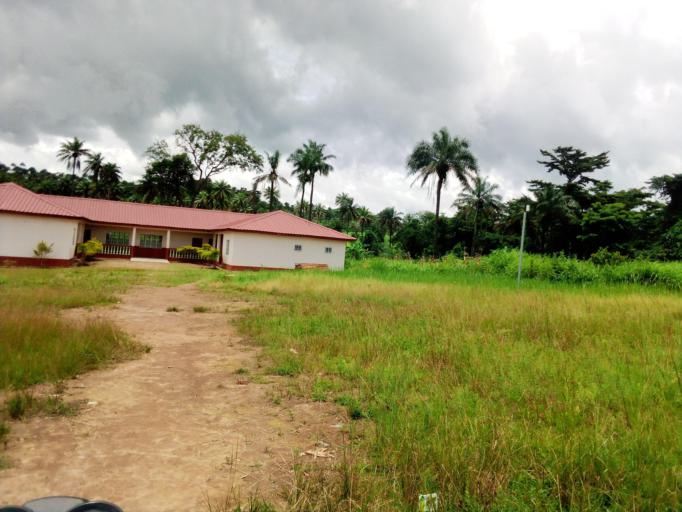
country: SL
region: Eastern Province
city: Giehun
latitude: 8.5576
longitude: -10.9850
